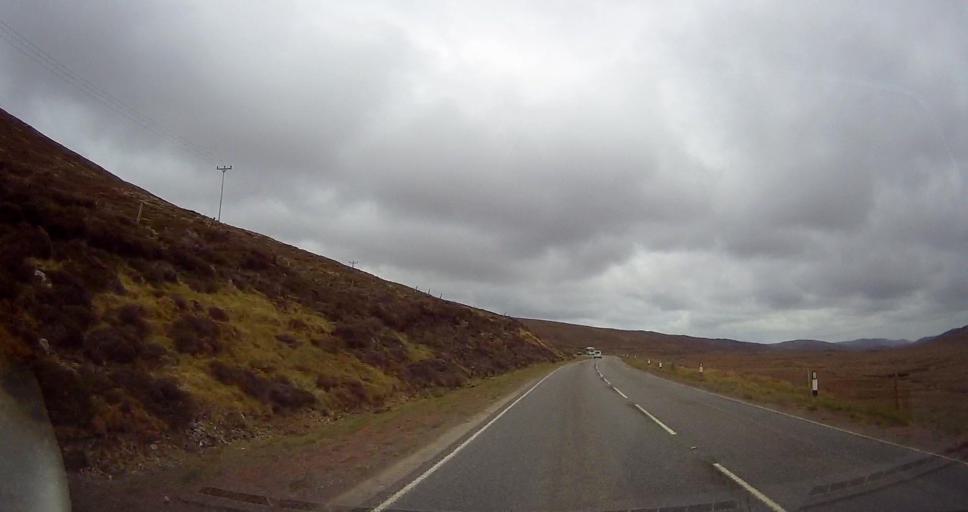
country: GB
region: Scotland
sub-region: Shetland Islands
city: Lerwick
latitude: 60.3110
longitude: -1.2464
